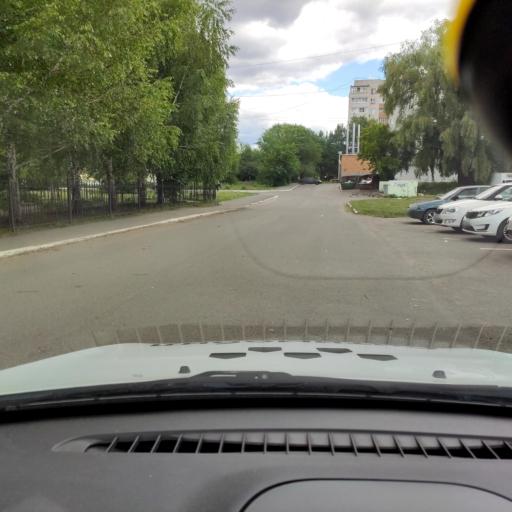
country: RU
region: Samara
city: Zhigulevsk
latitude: 53.4014
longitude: 49.5120
